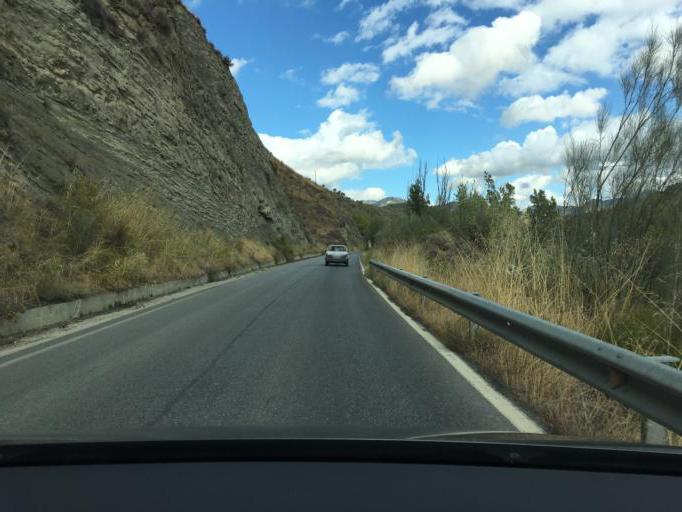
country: ES
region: Andalusia
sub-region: Provincia de Granada
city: Pinos Genil
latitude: 37.1759
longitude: -3.5039
